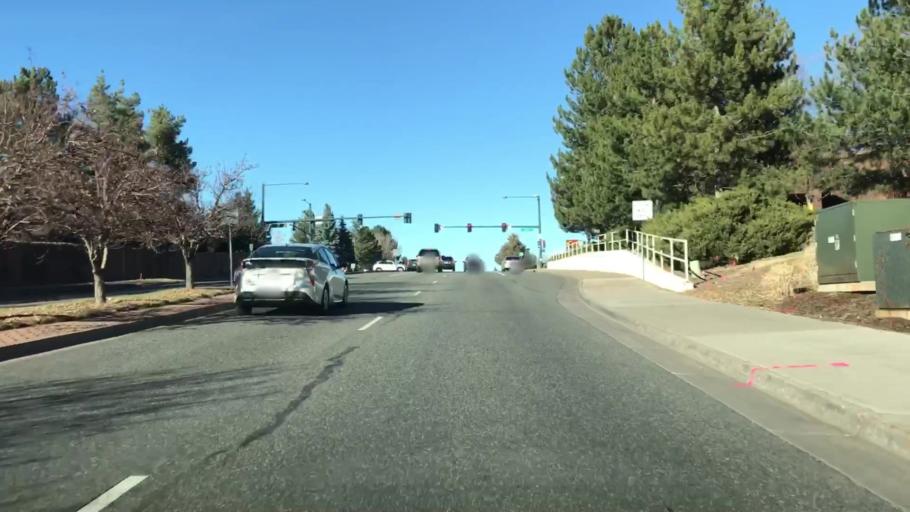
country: US
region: Colorado
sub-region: Arapahoe County
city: Castlewood
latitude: 39.6304
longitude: -104.8851
